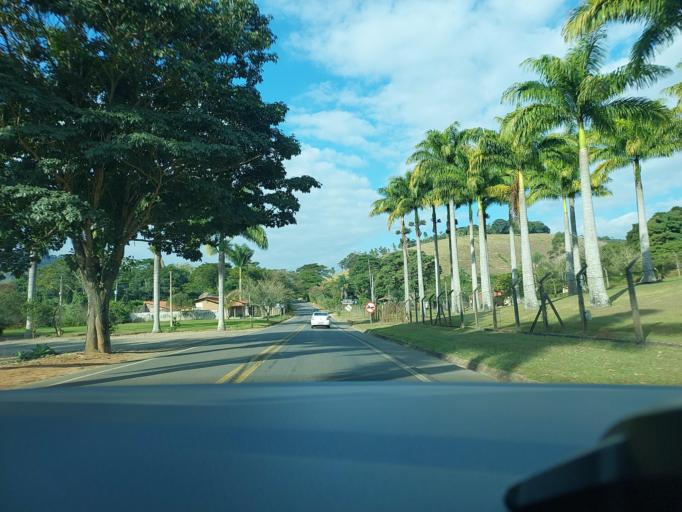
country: BR
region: Minas Gerais
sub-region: Vicosa
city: Vicosa
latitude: -20.8274
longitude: -42.7796
